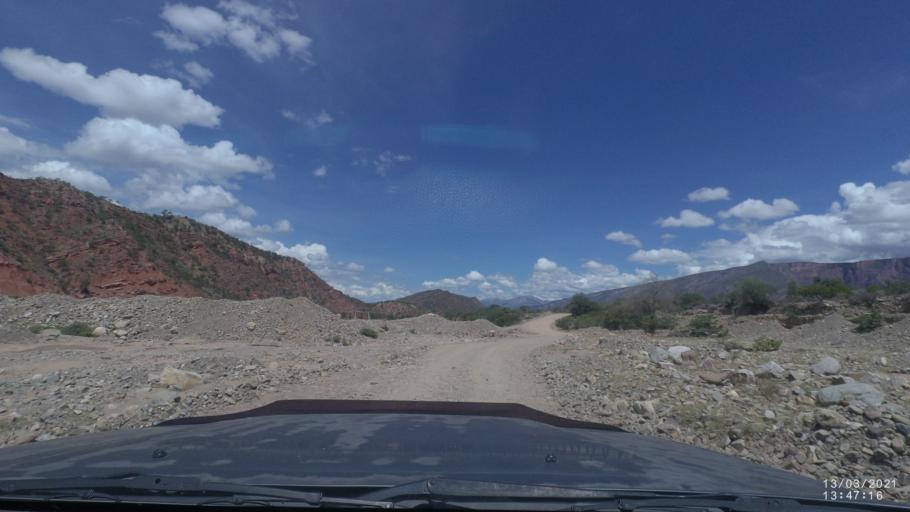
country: BO
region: Cochabamba
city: Cliza
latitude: -17.9328
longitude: -65.8678
